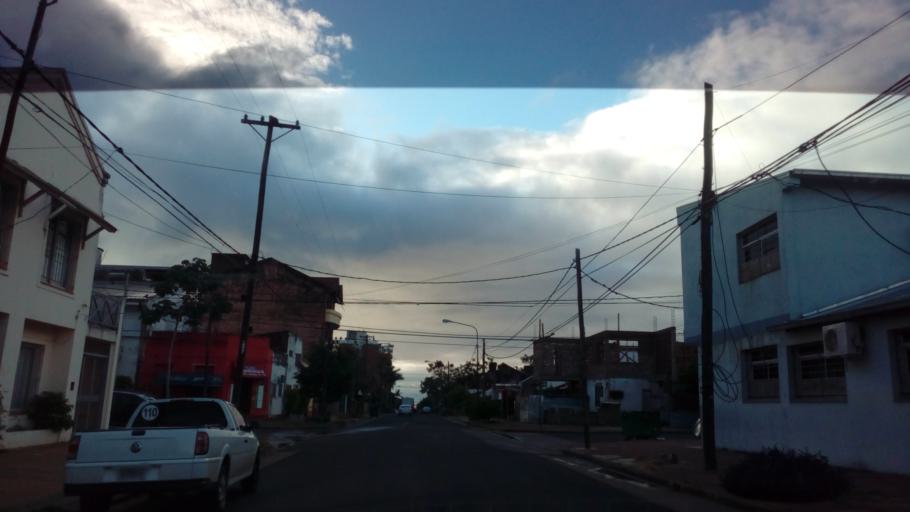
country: AR
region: Misiones
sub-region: Departamento de Capital
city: Posadas
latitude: -27.3543
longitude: -55.8947
